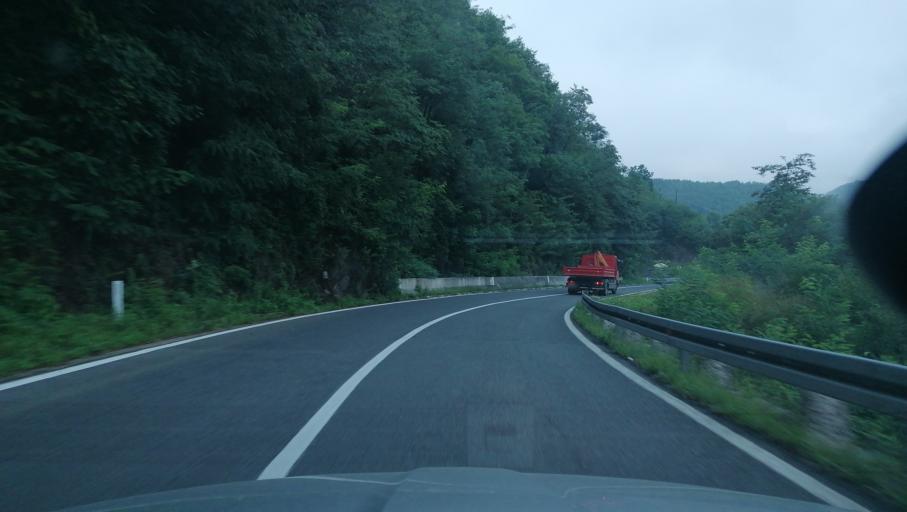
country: BA
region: Federation of Bosnia and Herzegovina
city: Jablanica
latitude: 43.7193
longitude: 17.7096
